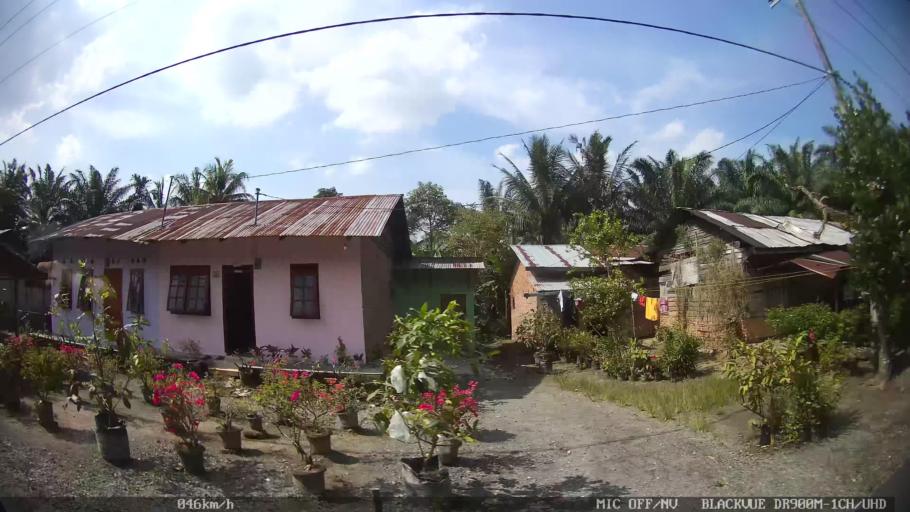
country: ID
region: North Sumatra
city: Binjai
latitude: 3.6345
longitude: 98.5249
